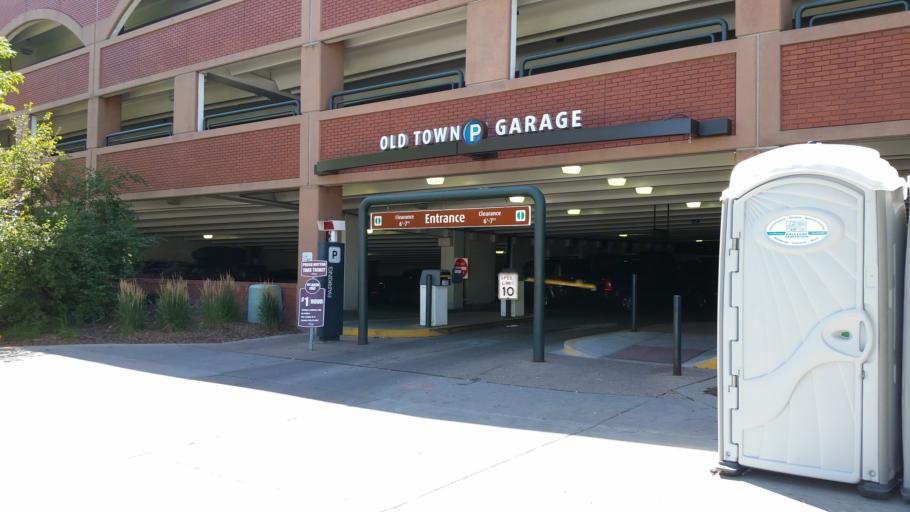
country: US
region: Colorado
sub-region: Larimer County
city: Fort Collins
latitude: 40.5869
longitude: -105.0752
